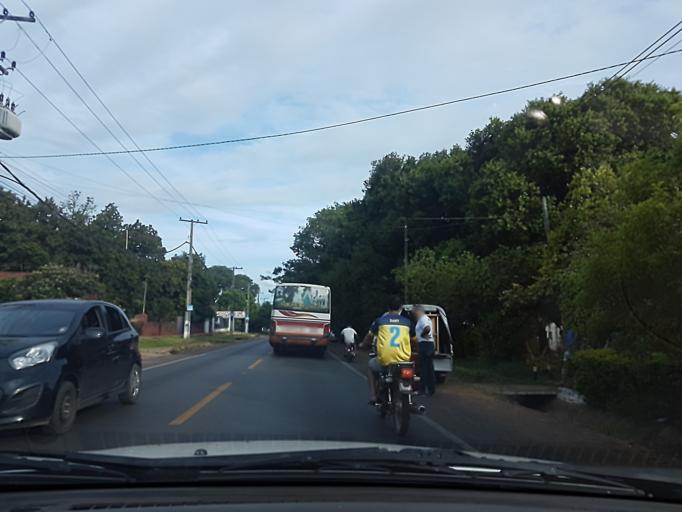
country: PY
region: Central
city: San Lorenzo
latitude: -25.2813
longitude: -57.4714
